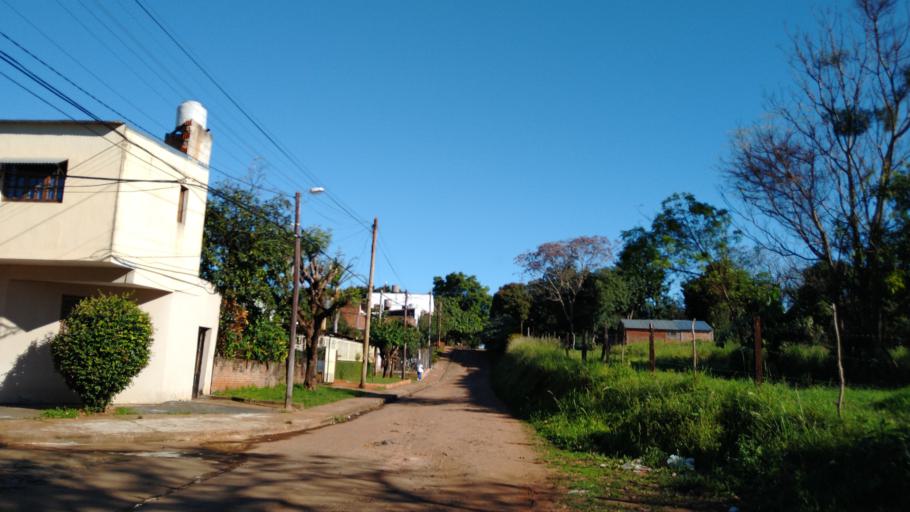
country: AR
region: Misiones
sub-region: Departamento de Capital
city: Posadas
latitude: -27.3631
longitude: -55.9292
